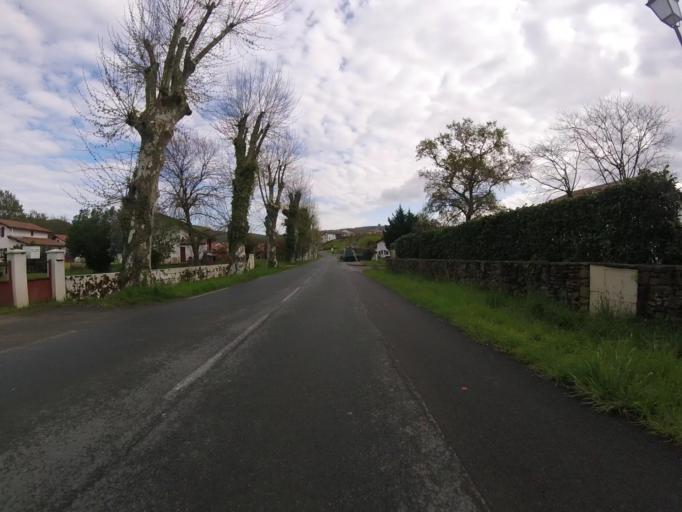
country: FR
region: Aquitaine
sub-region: Departement des Pyrenees-Atlantiques
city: Sare
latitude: 43.3102
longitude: -1.5850
